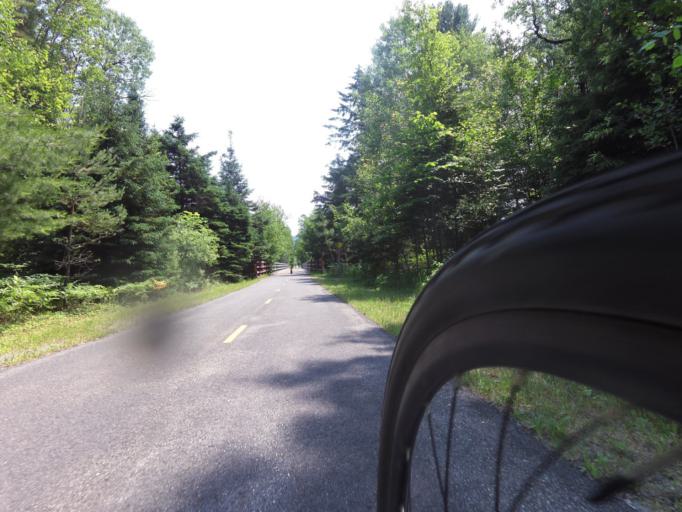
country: CA
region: Quebec
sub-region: Laurentides
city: Mont-Tremblant
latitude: 46.1548
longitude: -74.5993
